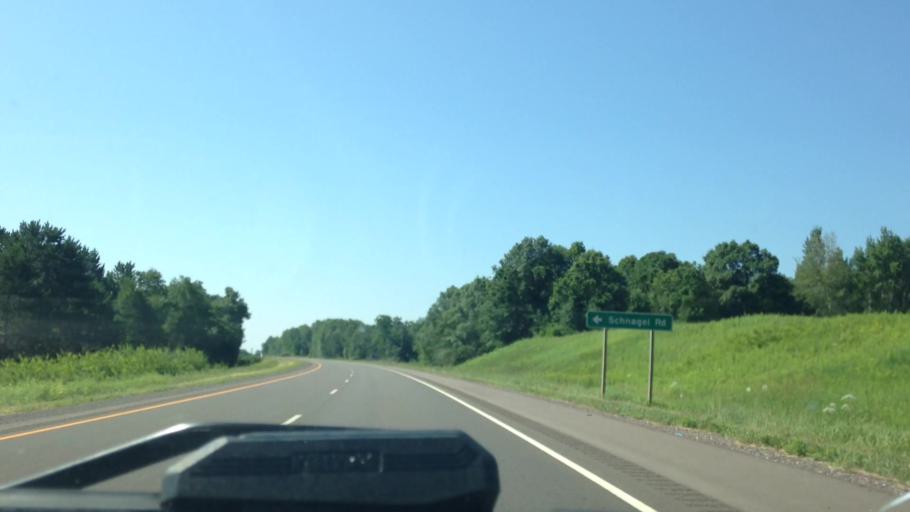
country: US
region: Wisconsin
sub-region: Washburn County
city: Spooner
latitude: 45.9454
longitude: -91.8293
